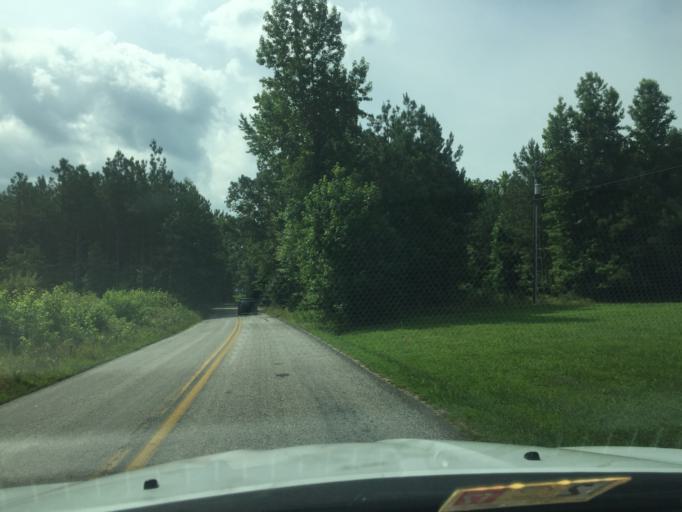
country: US
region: Virginia
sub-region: Charles City County
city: Charles City
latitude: 37.3869
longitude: -77.0124
